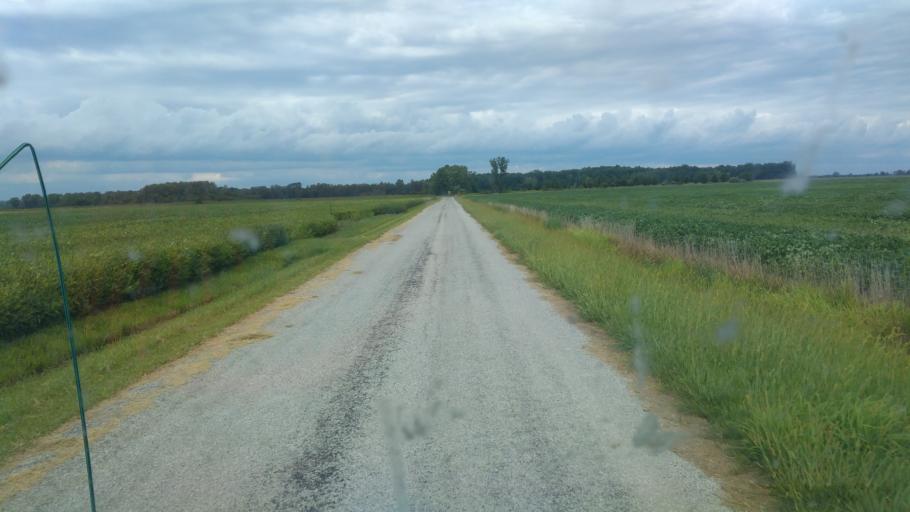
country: US
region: Ohio
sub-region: Wyandot County
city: Upper Sandusky
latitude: 40.6988
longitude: -83.2655
